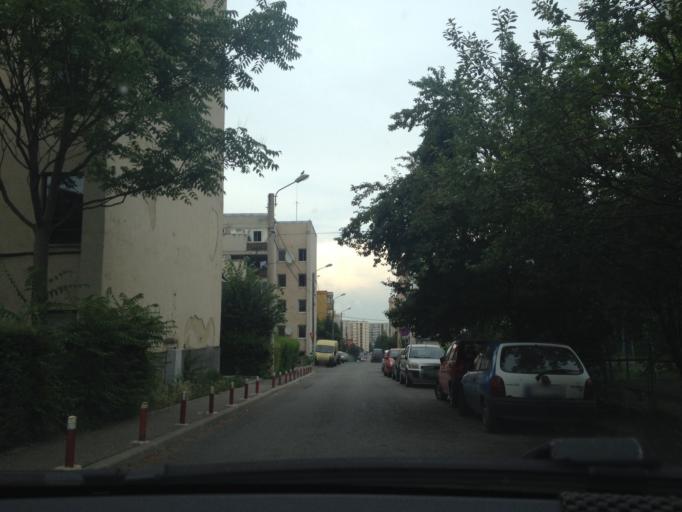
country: RO
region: Cluj
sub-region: Municipiul Cluj-Napoca
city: Cluj-Napoca
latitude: 46.7520
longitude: 23.5505
